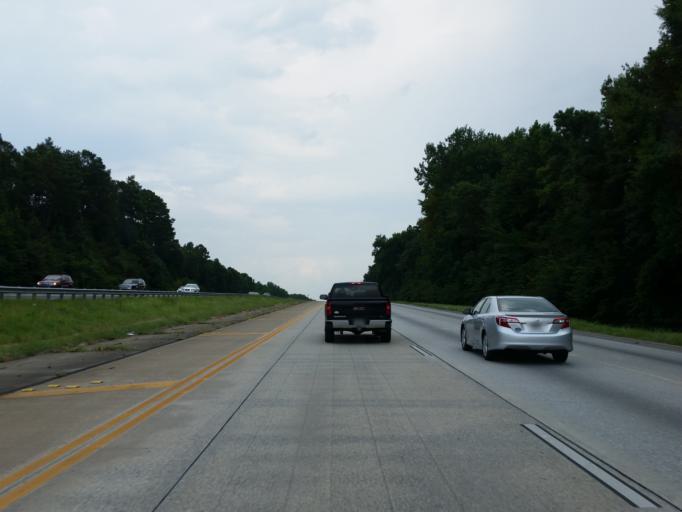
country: US
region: Georgia
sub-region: Monroe County
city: Forsyth
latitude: 33.0210
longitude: -83.8967
